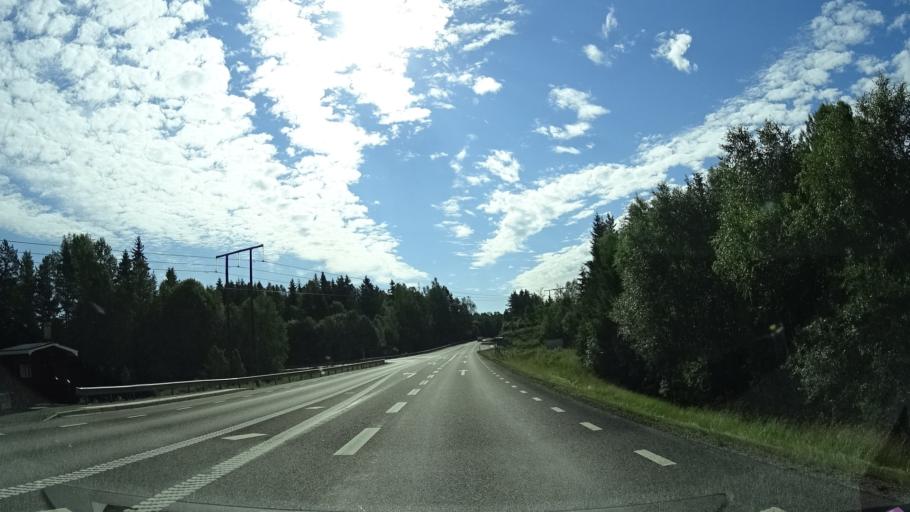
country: SE
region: Vaermland
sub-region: Arjangs Kommun
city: Toecksfors
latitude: 59.4969
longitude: 11.9163
